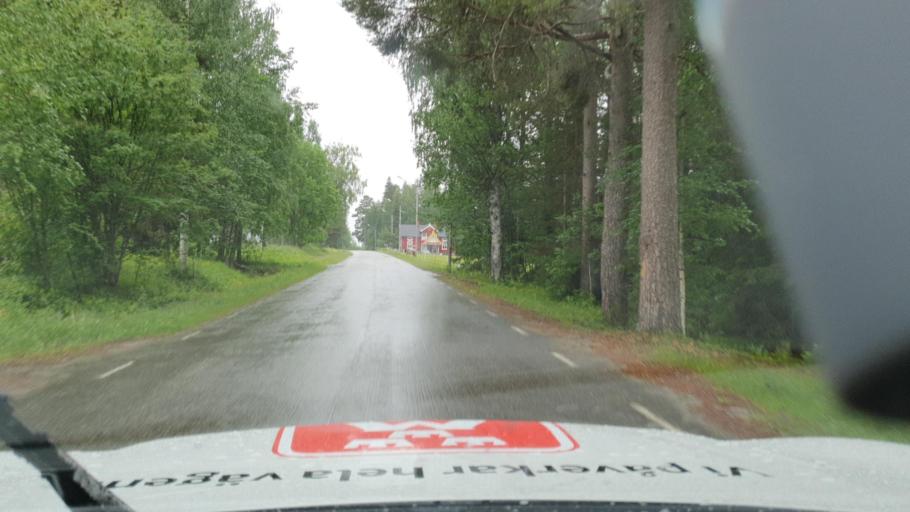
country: SE
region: Vaesterbotten
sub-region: Lycksele Kommun
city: Lycksele
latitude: 64.0758
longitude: 18.3606
